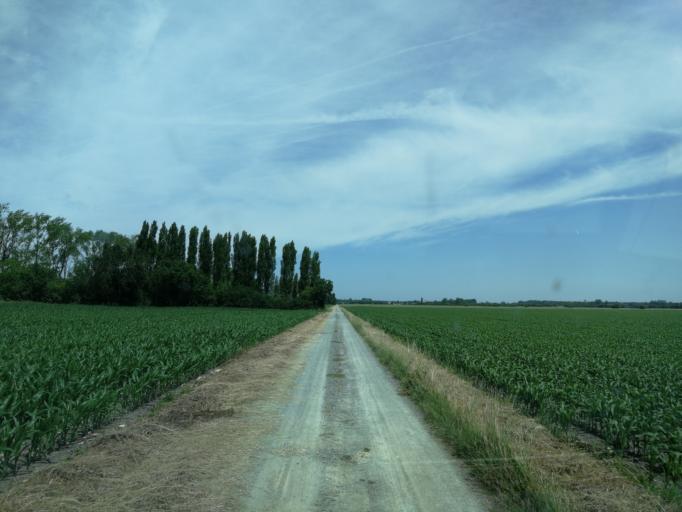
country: FR
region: Pays de la Loire
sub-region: Departement de la Vendee
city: Le Langon
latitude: 46.3691
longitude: -0.9587
